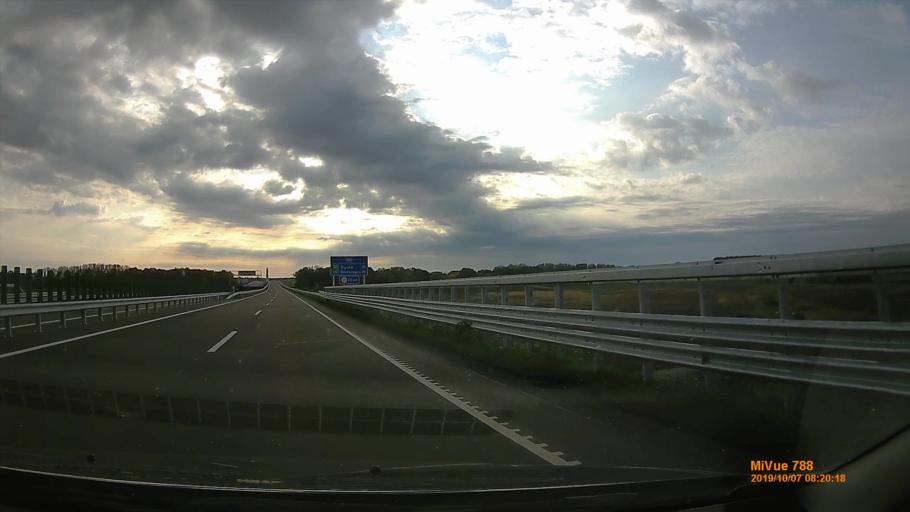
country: HU
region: Jasz-Nagykun-Szolnok
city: Kunszentmarton
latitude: 46.8672
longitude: 20.2781
